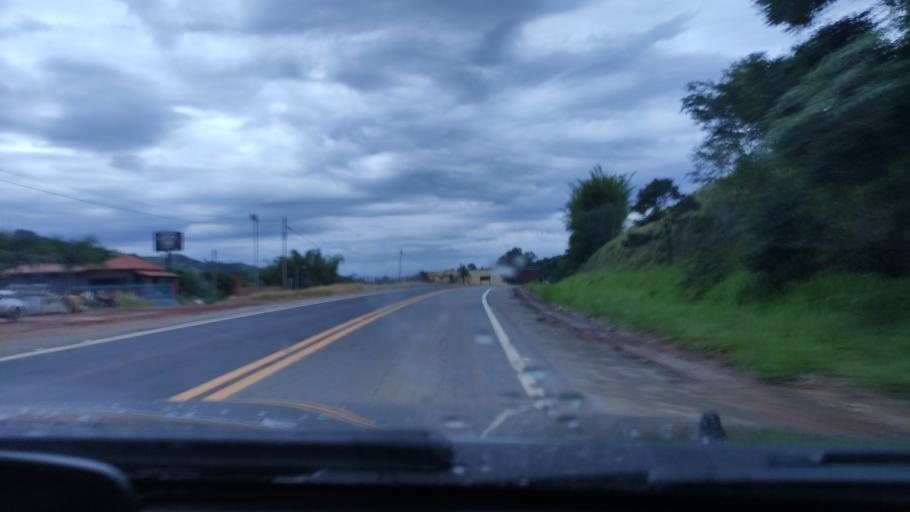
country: BR
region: Sao Paulo
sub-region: Socorro
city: Socorro
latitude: -22.6398
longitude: -46.5370
